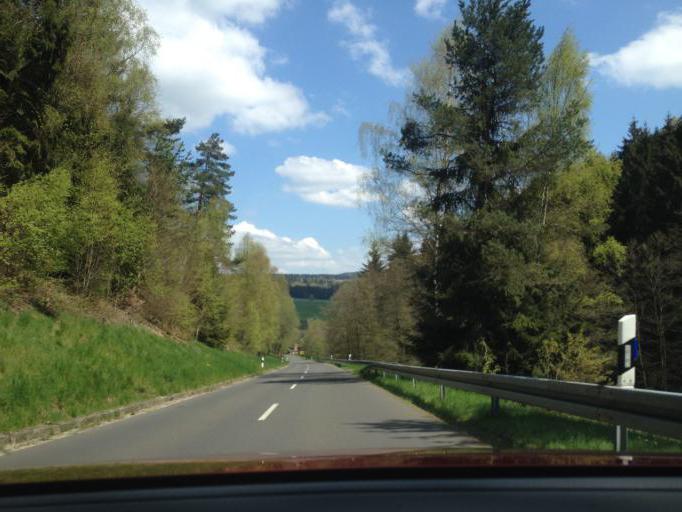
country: DE
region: Bavaria
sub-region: Upper Palatinate
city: Neusorg
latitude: 49.8862
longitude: 11.9658
